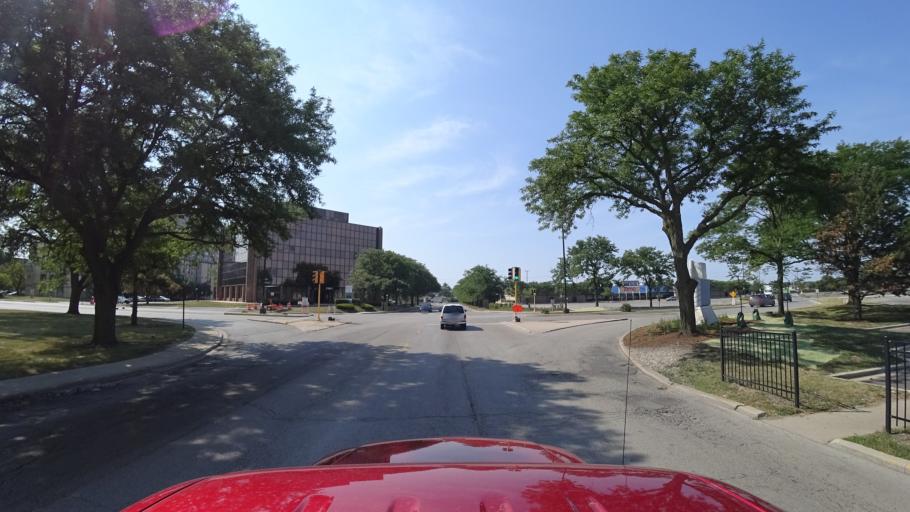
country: US
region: Illinois
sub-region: Cook County
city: Hometown
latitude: 41.7554
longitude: -87.7324
